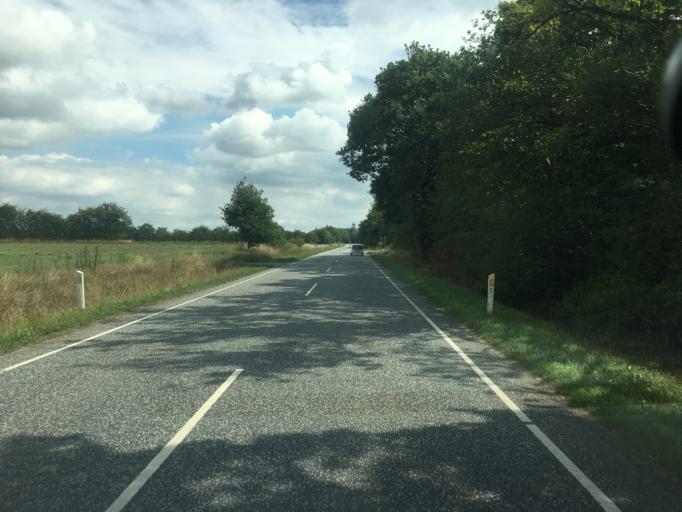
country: DK
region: South Denmark
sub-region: Aabenraa Kommune
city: Aabenraa
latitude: 54.9817
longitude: 9.3575
